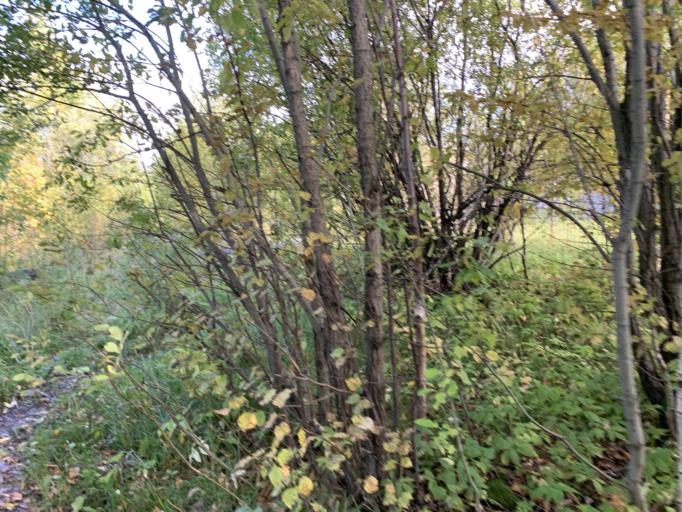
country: RU
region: Perm
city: Gubakha
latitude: 58.8370
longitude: 57.5587
